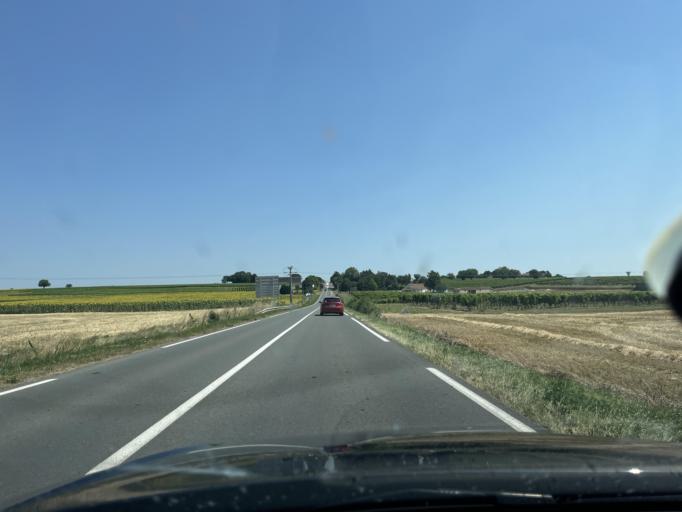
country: FR
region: Poitou-Charentes
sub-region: Departement de la Charente-Maritime
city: Mortagne-sur-Gironde
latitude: 45.4628
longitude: -0.7000
